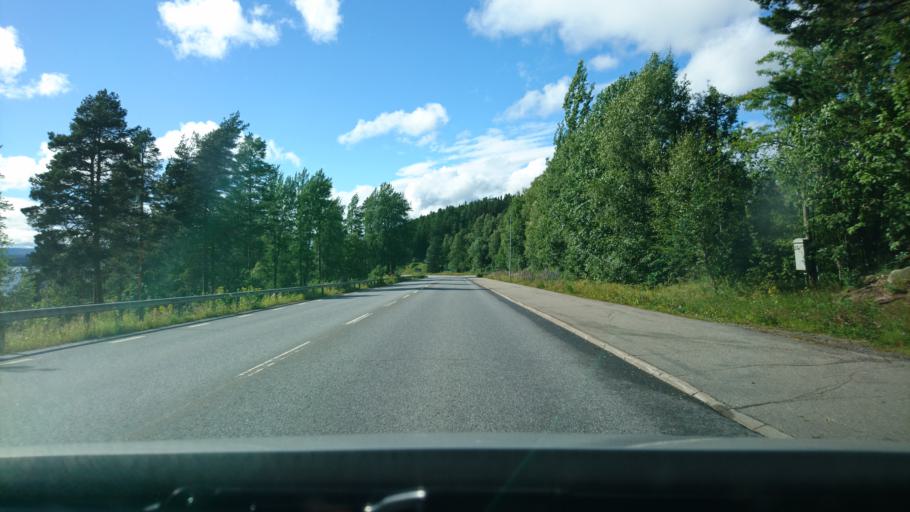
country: SE
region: Vaesterbotten
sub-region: Vilhelmina Kommun
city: Vilhelmina
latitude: 64.6299
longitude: 16.6418
